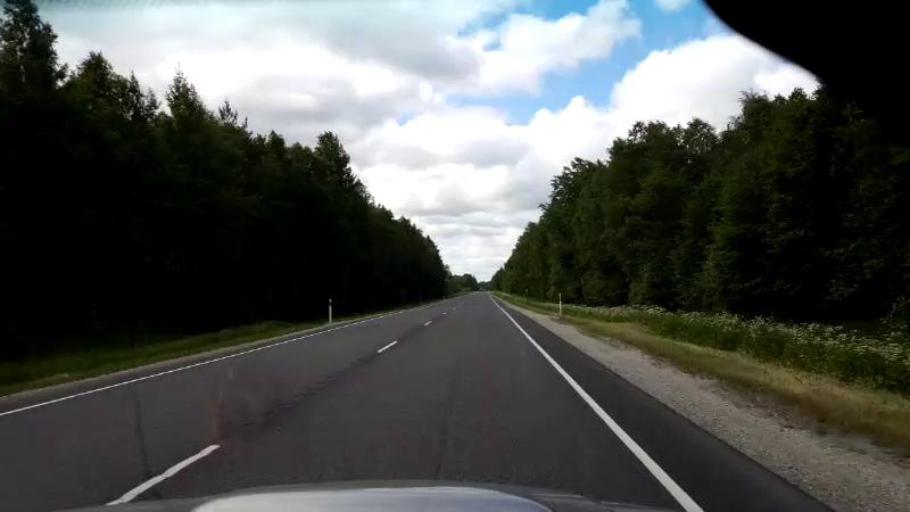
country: EE
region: Raplamaa
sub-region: Maerjamaa vald
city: Marjamaa
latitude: 58.8374
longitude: 24.4220
